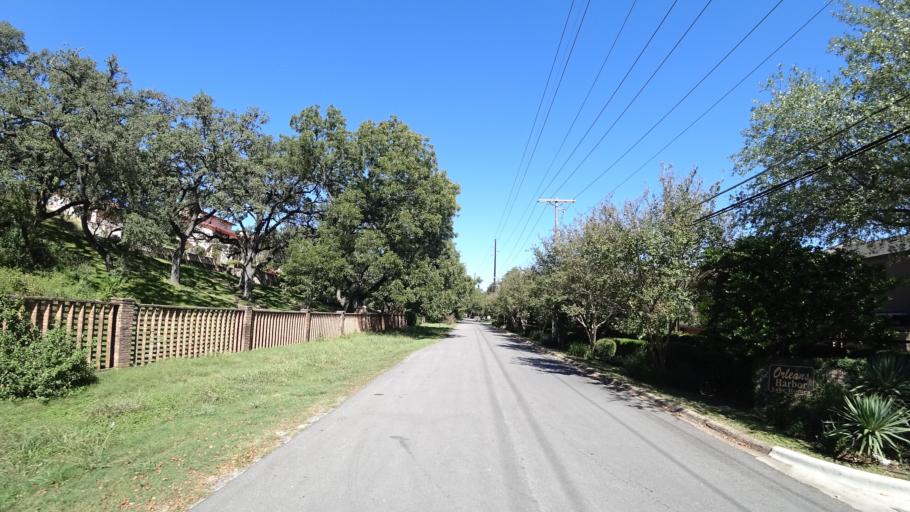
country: US
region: Texas
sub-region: Travis County
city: West Lake Hills
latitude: 30.3049
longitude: -97.7833
